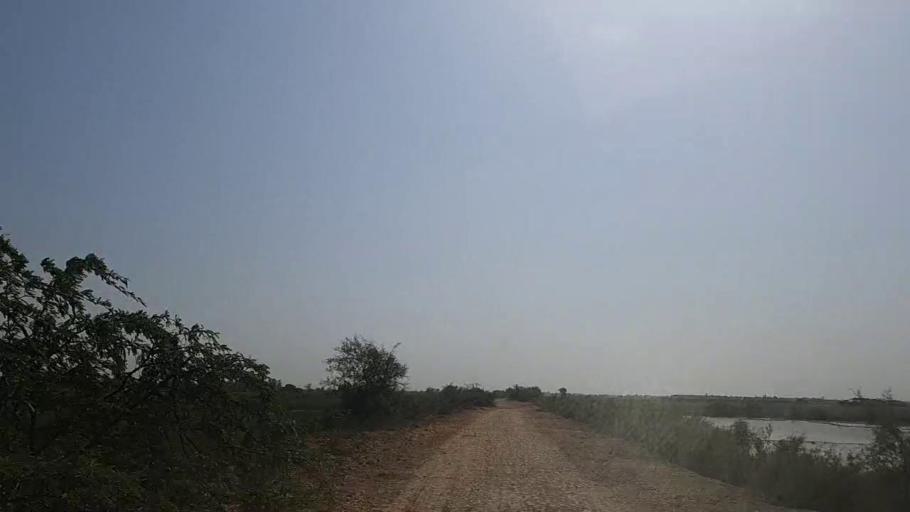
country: PK
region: Sindh
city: Daro Mehar
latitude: 24.7138
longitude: 68.1204
